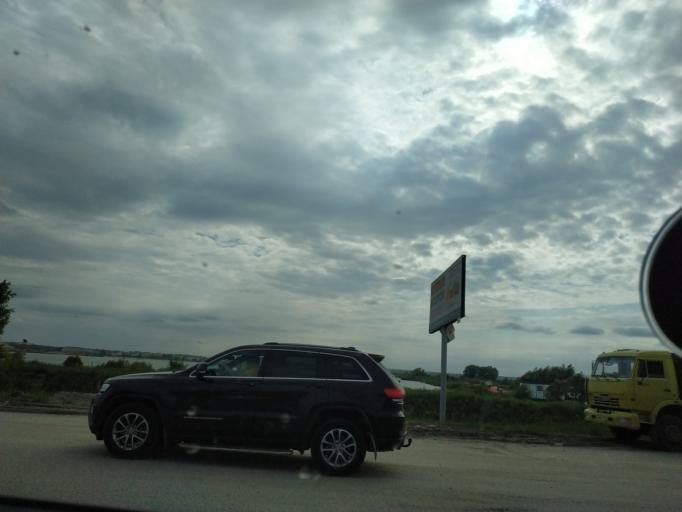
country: RU
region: Moskovskaya
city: Ramenskoye
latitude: 55.5117
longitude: 38.2802
